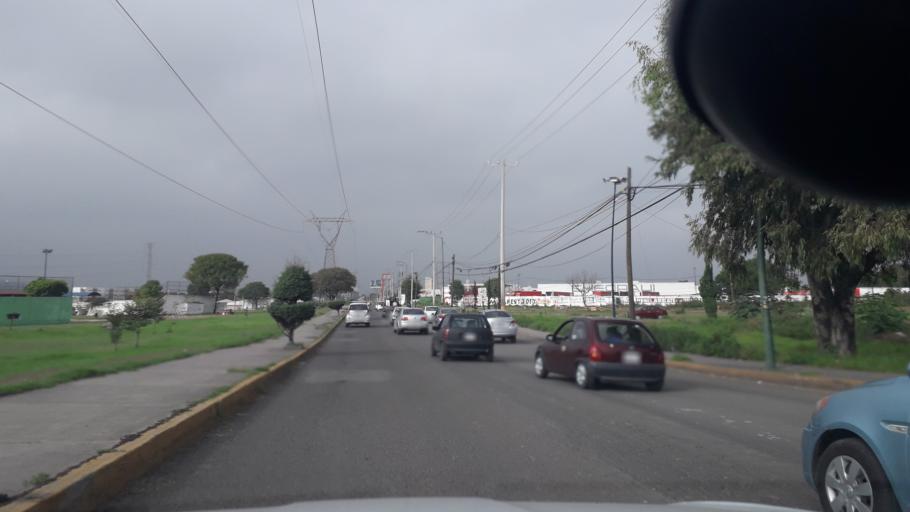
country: MX
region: Mexico
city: Coacalco
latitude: 19.6449
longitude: -99.1047
